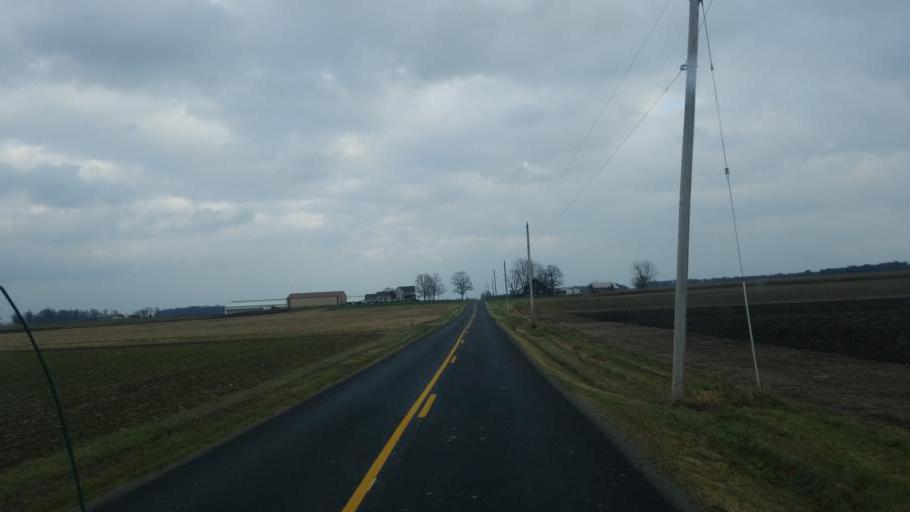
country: US
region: Ohio
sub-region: Mercer County
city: Fort Recovery
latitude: 40.5090
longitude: -84.7382
